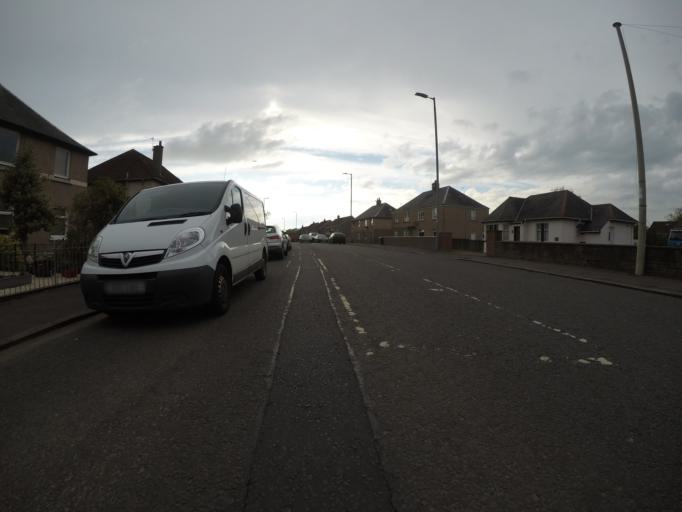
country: GB
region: Scotland
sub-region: North Ayrshire
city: Dreghorn
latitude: 55.6069
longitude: -4.6257
